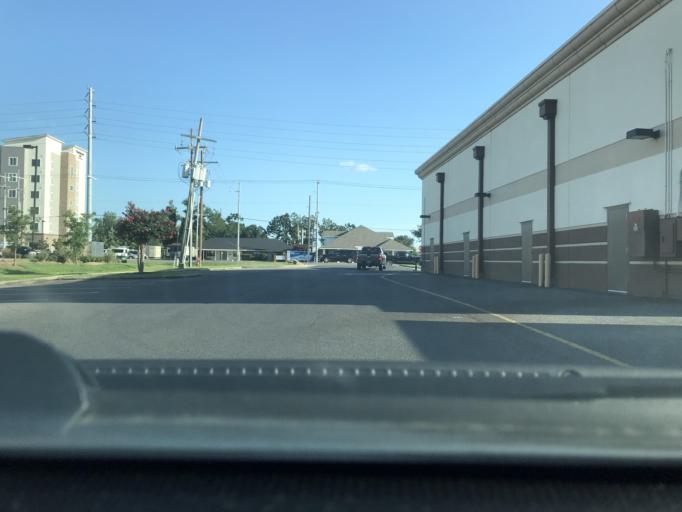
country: US
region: Louisiana
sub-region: Calcasieu Parish
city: Prien
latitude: 30.1984
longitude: -93.2456
